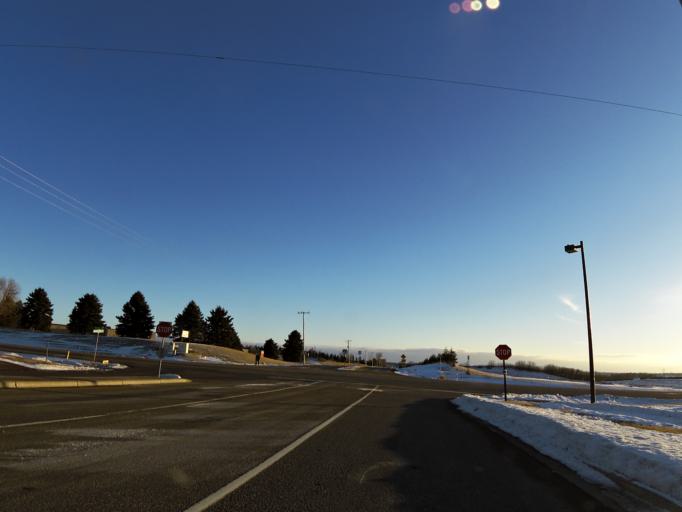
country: US
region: Minnesota
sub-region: Washington County
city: Woodbury
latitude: 44.8912
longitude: -92.8831
